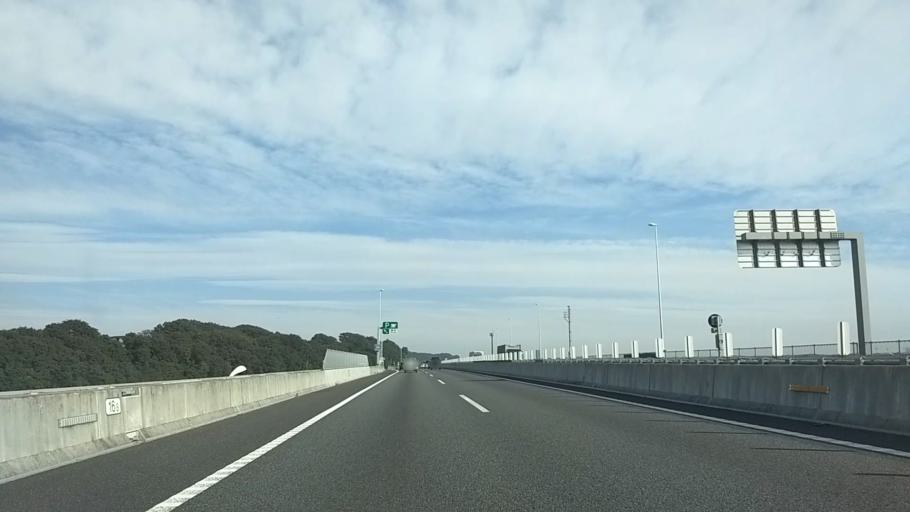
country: JP
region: Kanagawa
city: Zama
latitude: 35.4857
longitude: 139.3707
